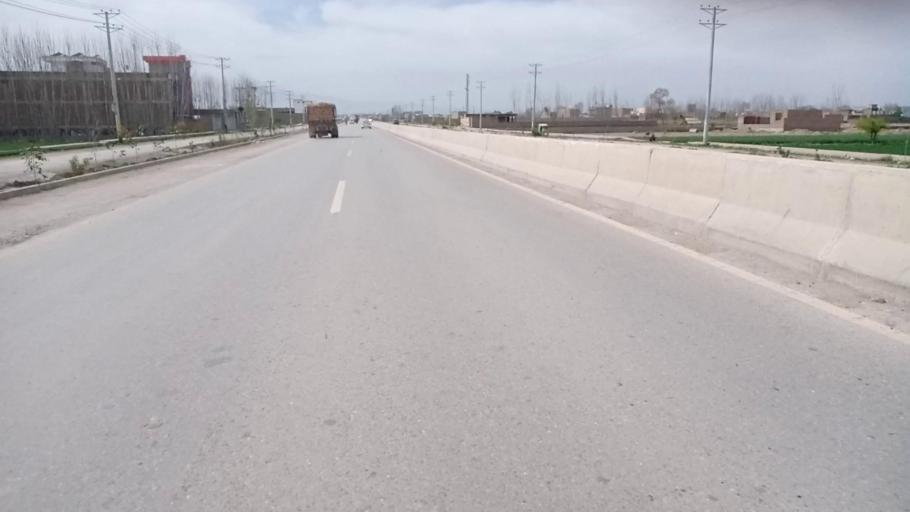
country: PK
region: Khyber Pakhtunkhwa
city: Peshawar
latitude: 34.0353
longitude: 71.6395
